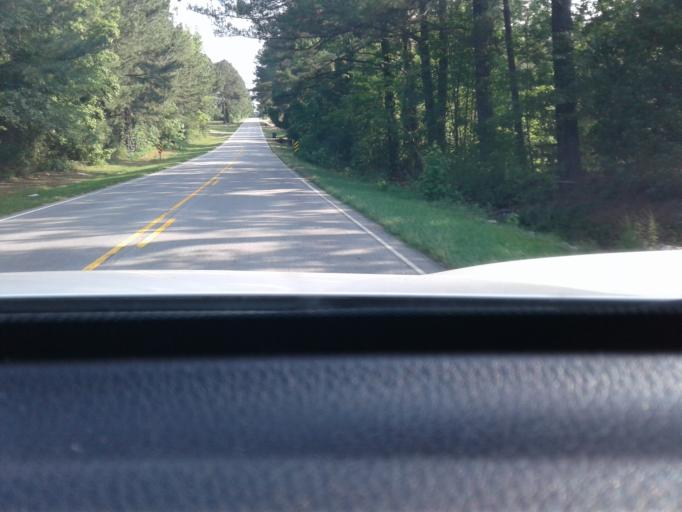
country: US
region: North Carolina
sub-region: Johnston County
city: Benson
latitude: 35.4065
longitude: -78.5406
